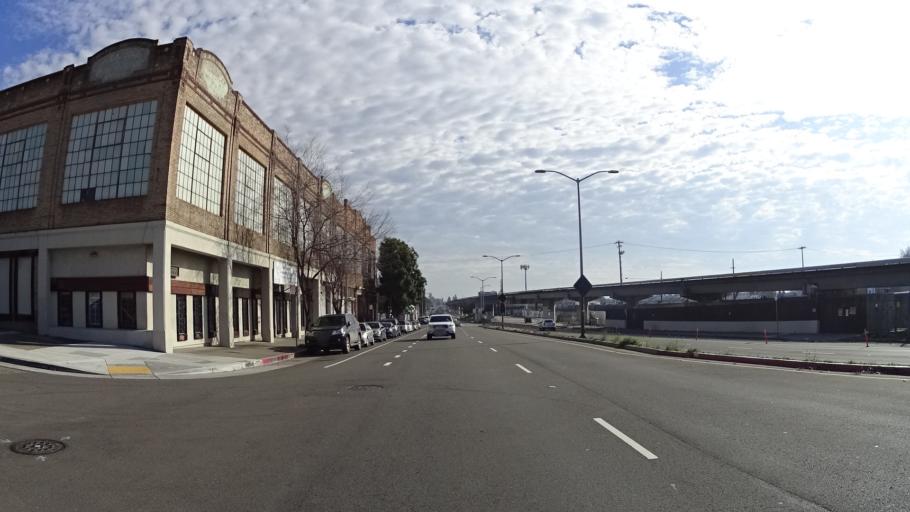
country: US
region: California
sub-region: Alameda County
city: Alameda
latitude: 37.7862
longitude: -122.2429
